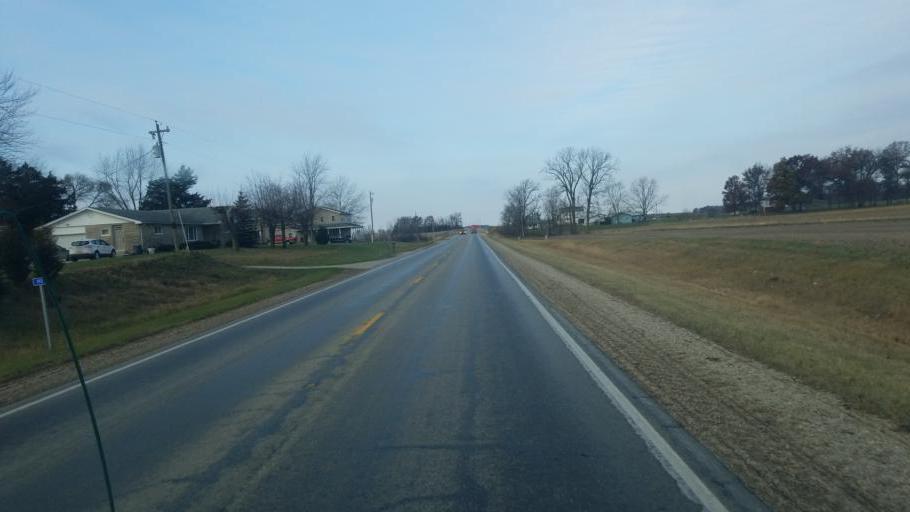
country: US
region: Indiana
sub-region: Adams County
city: Geneva
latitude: 40.5415
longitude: -84.9398
